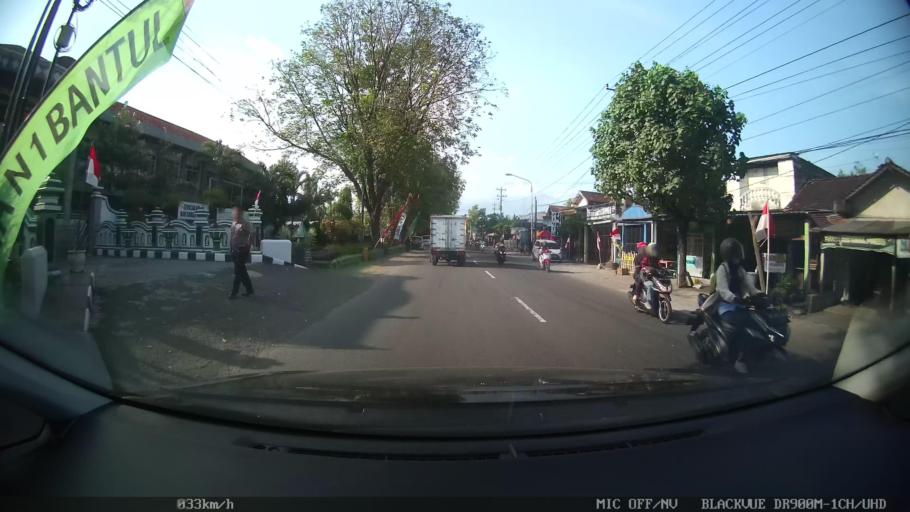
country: ID
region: Daerah Istimewa Yogyakarta
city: Bantul
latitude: -7.8985
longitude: 110.3226
